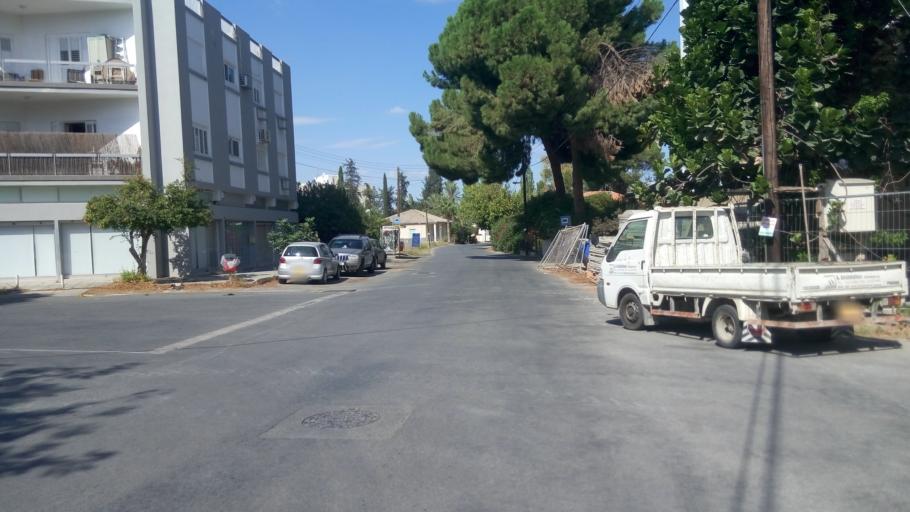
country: CY
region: Lefkosia
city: Nicosia
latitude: 35.1670
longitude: 33.3354
